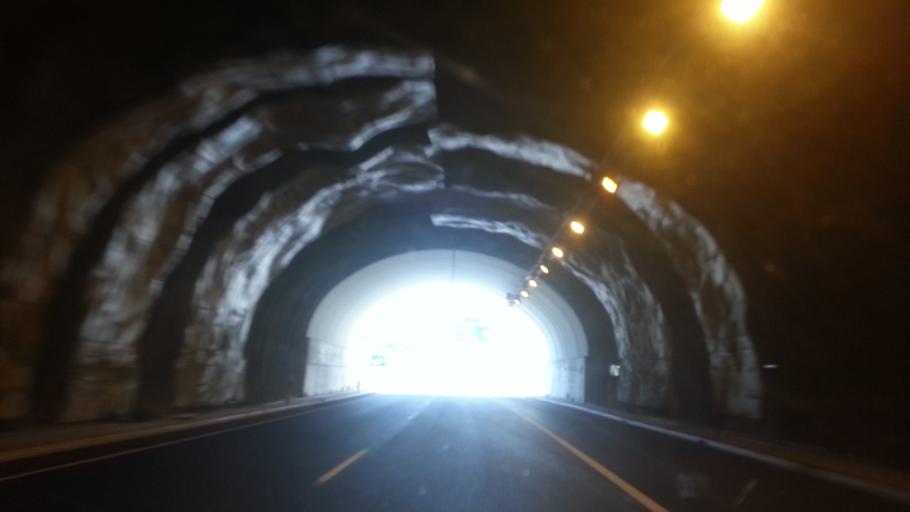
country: ES
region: Catalonia
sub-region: Provincia de Barcelona
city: Sant Pere de Ribes
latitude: 41.2847
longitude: 1.7289
